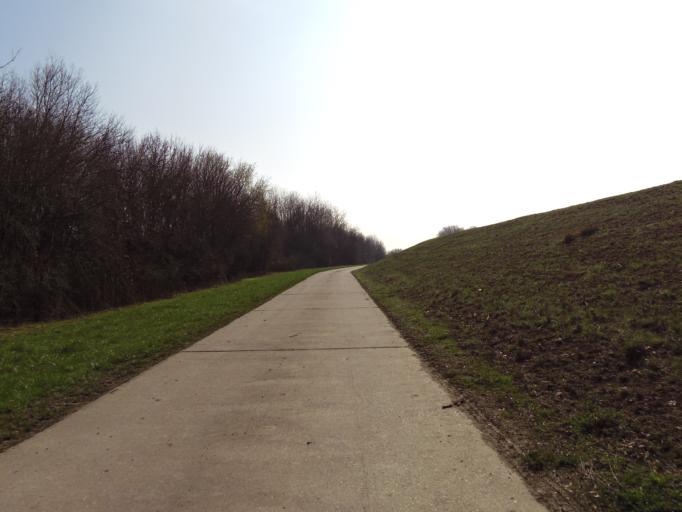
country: DE
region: Hesse
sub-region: Regierungsbezirk Darmstadt
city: Biblis
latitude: 49.7198
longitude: 8.4533
